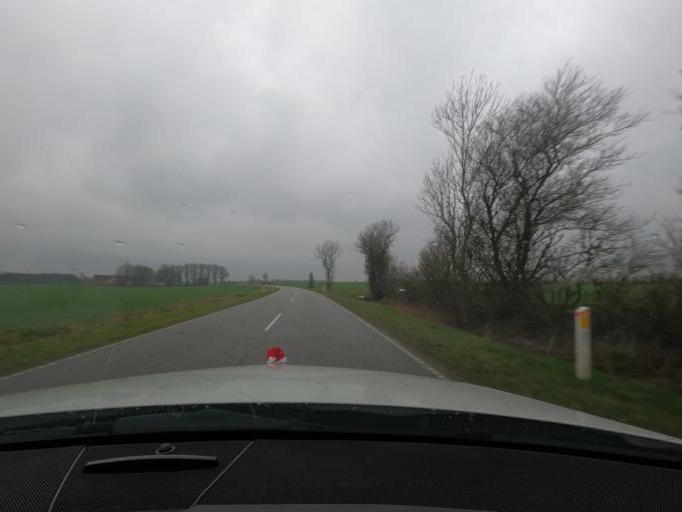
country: DK
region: South Denmark
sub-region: Haderslev Kommune
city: Starup
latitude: 55.2408
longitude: 9.6585
